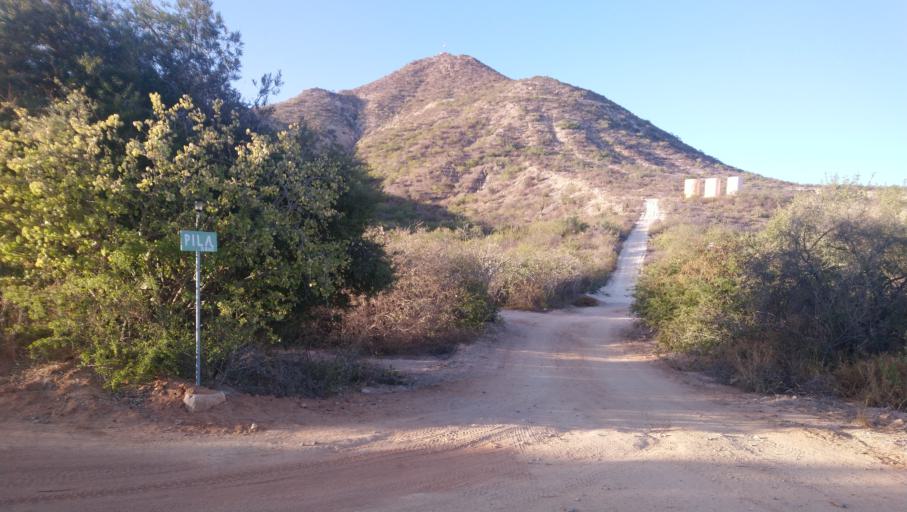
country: MX
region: Baja California Sur
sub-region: Los Cabos
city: Las Veredas
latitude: 23.4379
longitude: -109.4346
